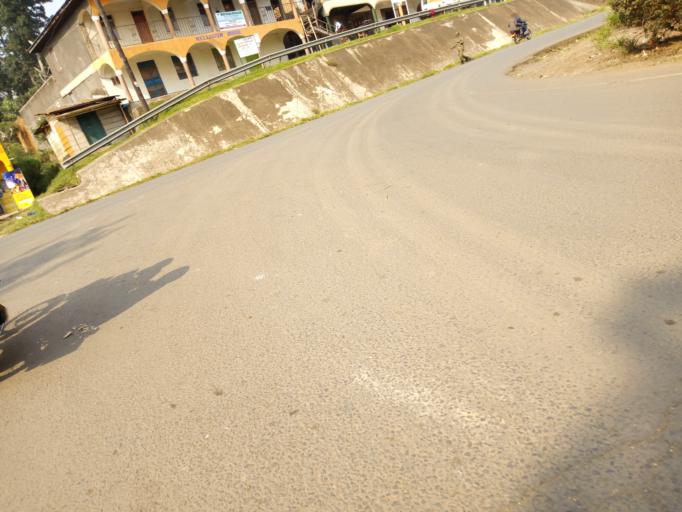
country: UG
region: Western Region
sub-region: Kisoro District
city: Kisoro
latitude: -1.2825
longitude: 29.6915
